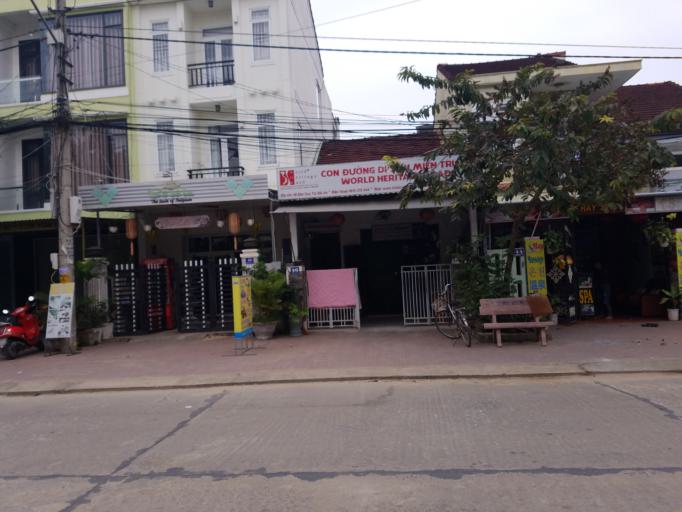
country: VN
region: Quang Nam
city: Hoi An
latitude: 15.8769
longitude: 108.3213
